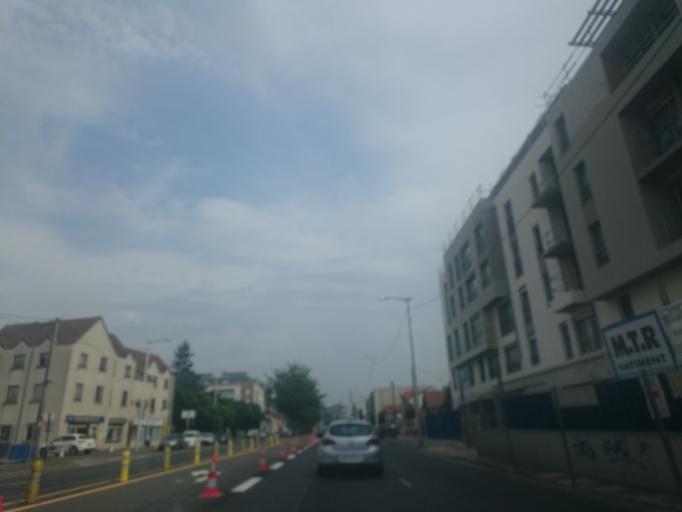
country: FR
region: Ile-de-France
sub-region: Departement de l'Essonne
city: Juvisy-sur-Orge
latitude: 48.6958
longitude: 2.3715
